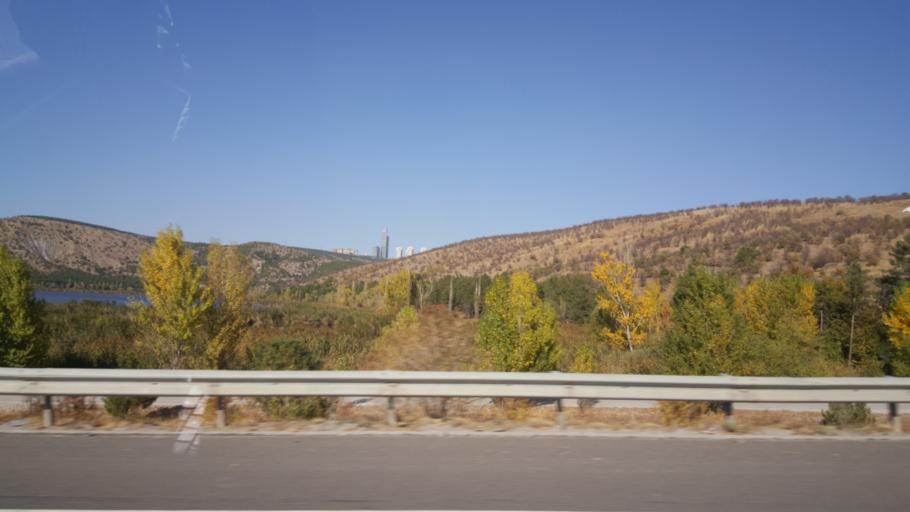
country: TR
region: Ankara
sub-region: Goelbasi
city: Golbasi
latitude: 39.8129
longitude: 32.8205
